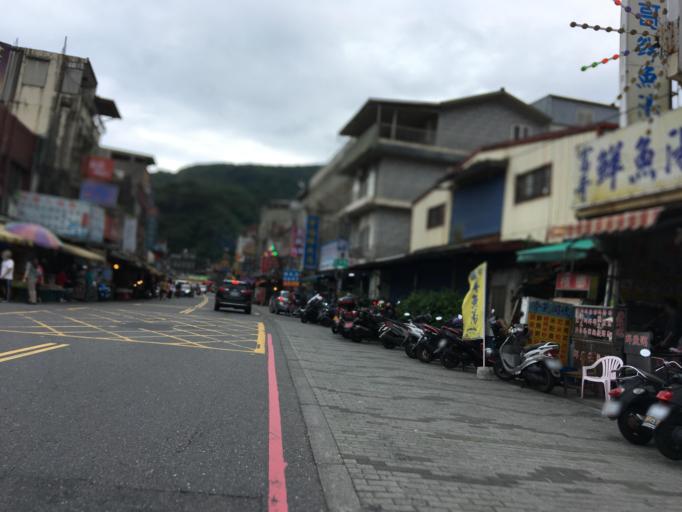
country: TW
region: Taiwan
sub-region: Yilan
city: Yilan
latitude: 24.5833
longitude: 121.8648
